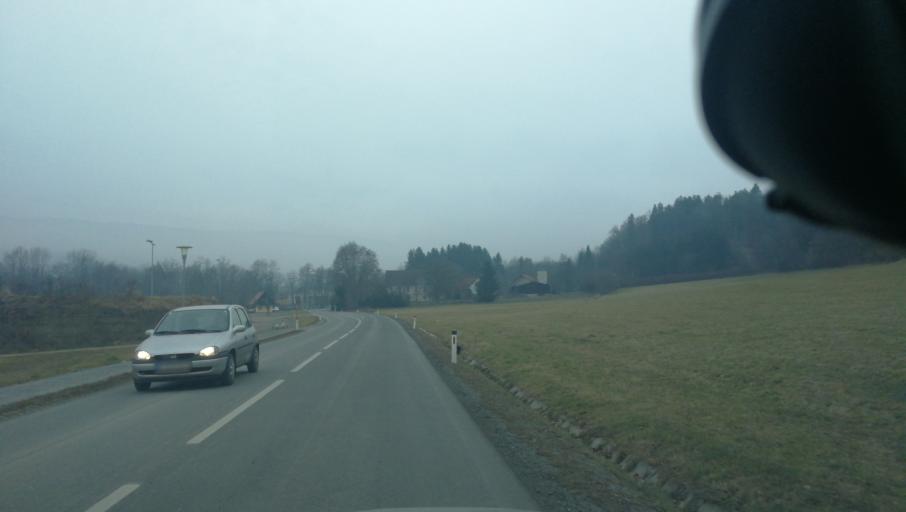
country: AT
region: Styria
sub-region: Politischer Bezirk Deutschlandsberg
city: Stainz
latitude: 46.8998
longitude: 15.2500
